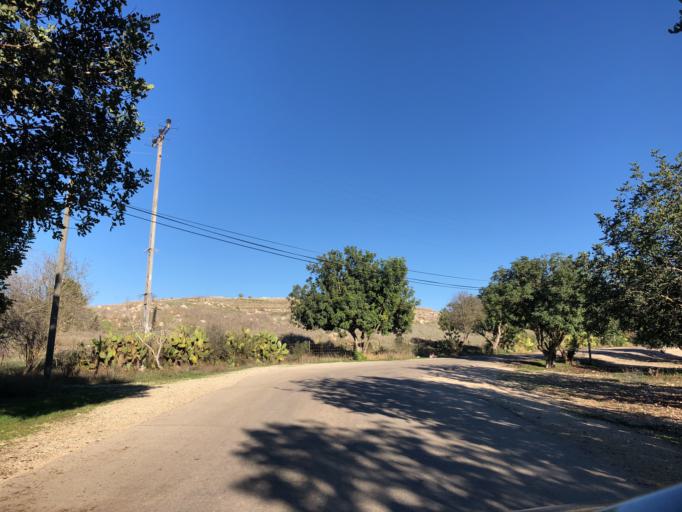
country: PS
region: West Bank
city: Idhna
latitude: 31.6039
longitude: 34.8972
